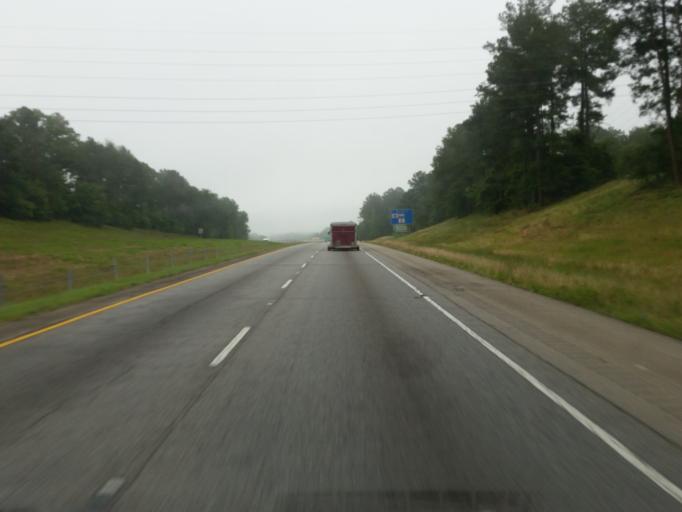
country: US
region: Louisiana
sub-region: Webster Parish
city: Minden
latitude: 32.5921
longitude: -93.3040
